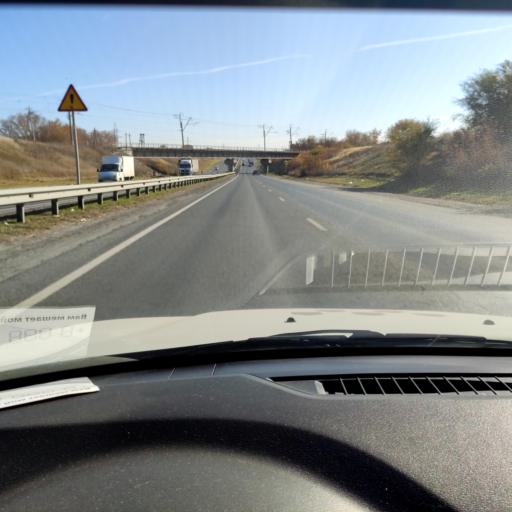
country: RU
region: Samara
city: Tol'yatti
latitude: 53.5697
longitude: 49.4797
